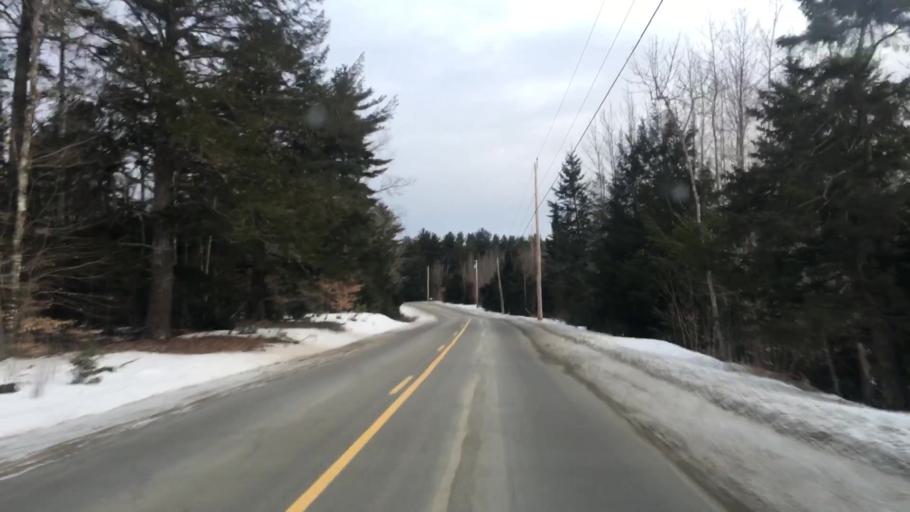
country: US
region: Maine
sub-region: Hancock County
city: Franklin
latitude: 44.7614
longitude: -68.3249
